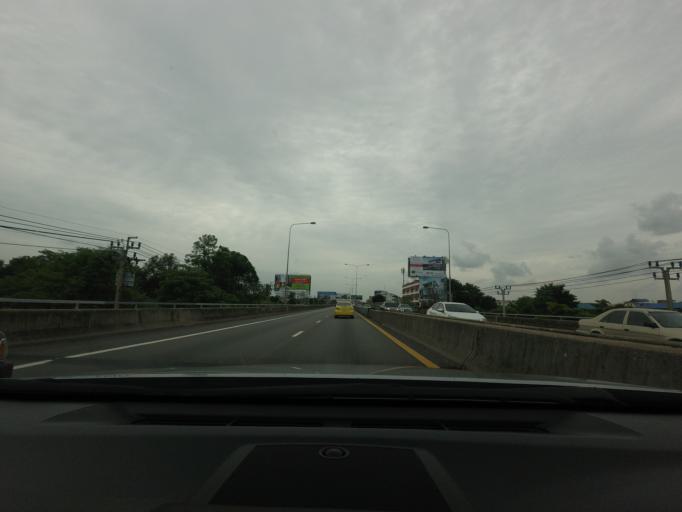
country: TH
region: Bangkok
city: Rat Burana
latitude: 13.6701
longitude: 100.5007
